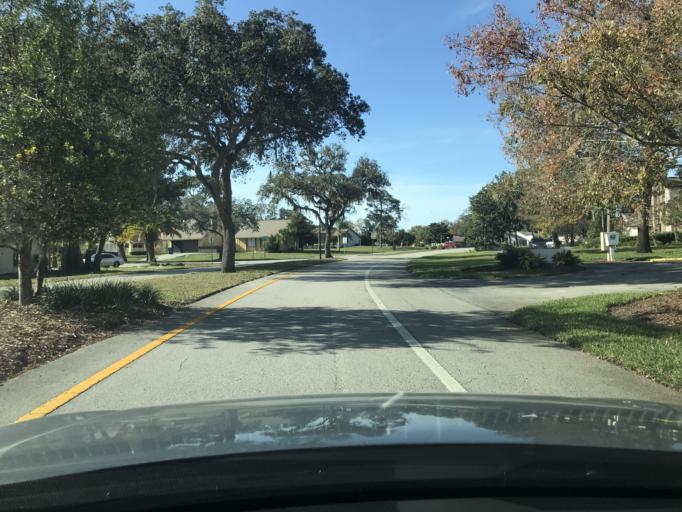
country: US
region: Florida
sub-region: Hernando County
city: North Weeki Wachee
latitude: 28.5374
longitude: -82.5733
